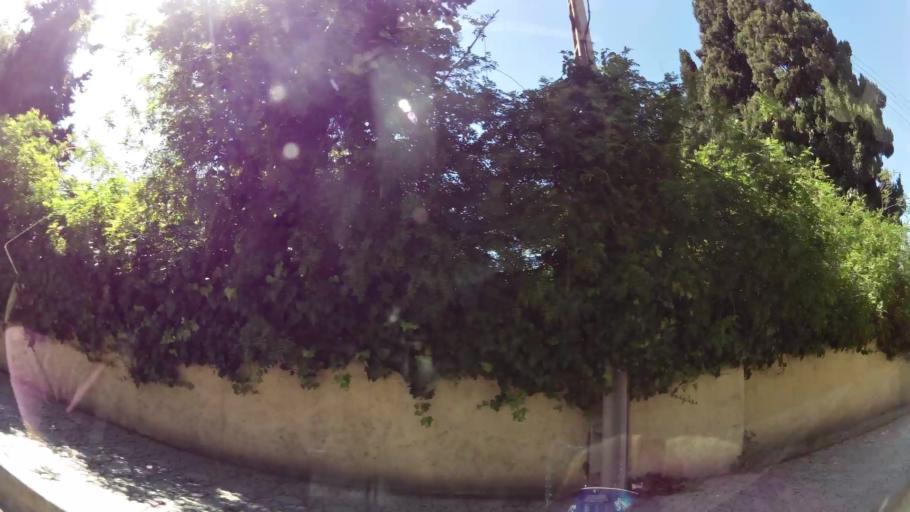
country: MA
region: Fes-Boulemane
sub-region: Fes
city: Fes
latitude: 34.0195
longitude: -4.9947
